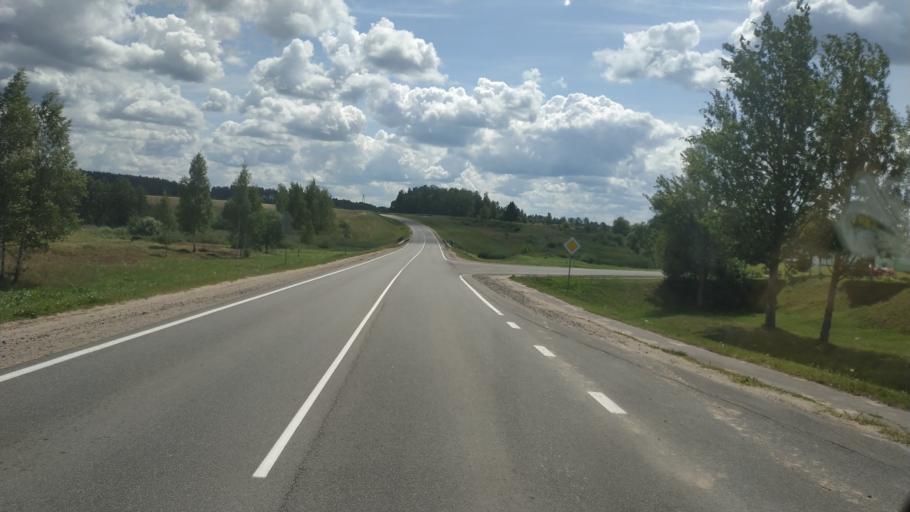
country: BY
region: Mogilev
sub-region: Mahilyowski Rayon
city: Veyno
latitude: 53.8369
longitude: 30.3990
